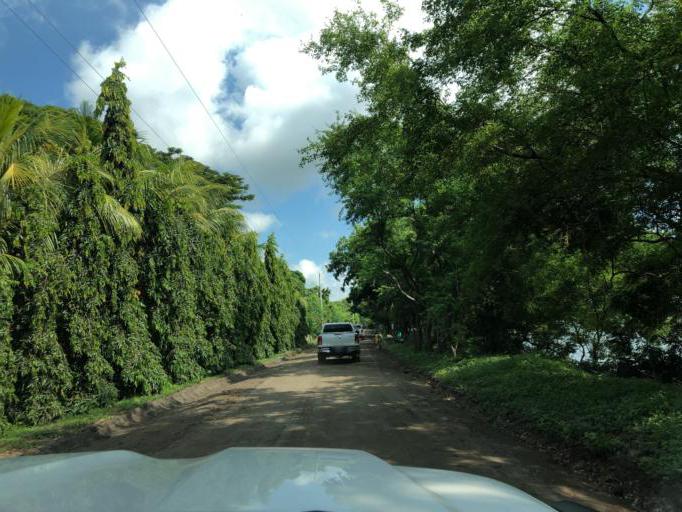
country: NI
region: Granada
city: Granada
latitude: 11.9883
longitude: -85.9389
